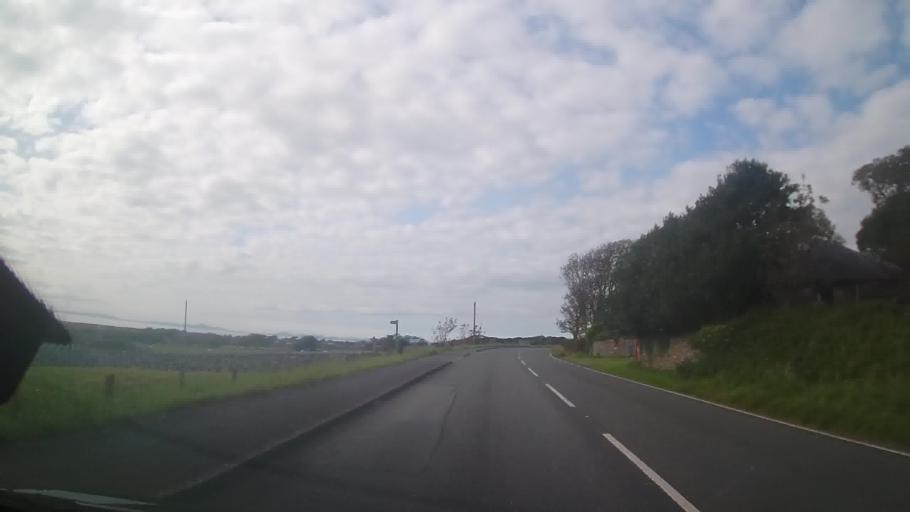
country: GB
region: Wales
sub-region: Gwynedd
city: Dyffryn Ardudwy
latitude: 52.7672
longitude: -4.0877
